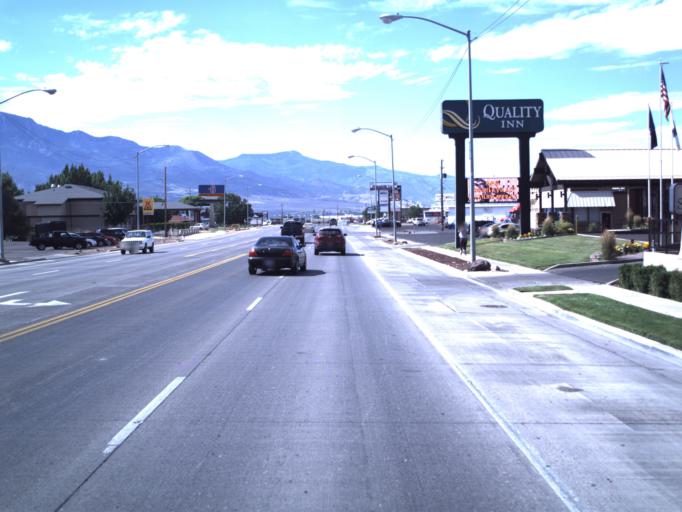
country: US
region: Utah
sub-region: Sevier County
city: Richfield
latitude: 38.7610
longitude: -112.0849
